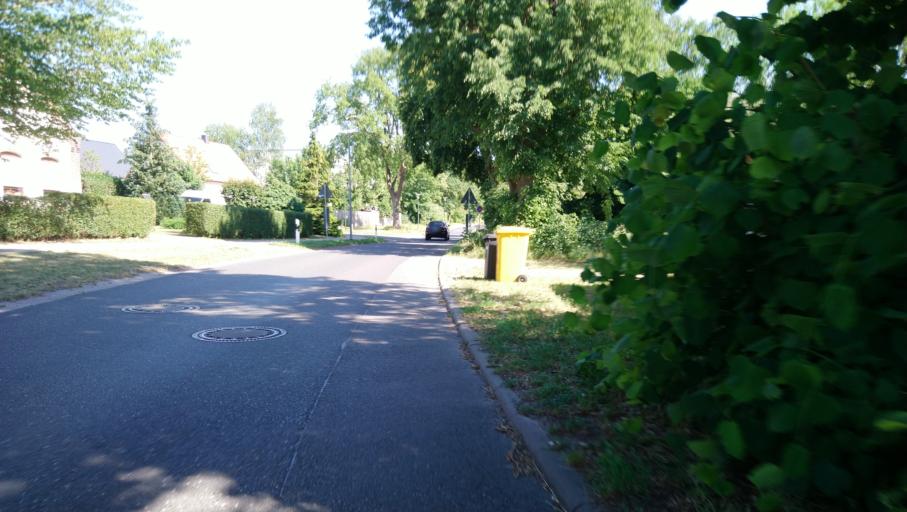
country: DE
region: Mecklenburg-Vorpommern
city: Dierkow-Neu
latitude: 54.0924
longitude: 12.1831
